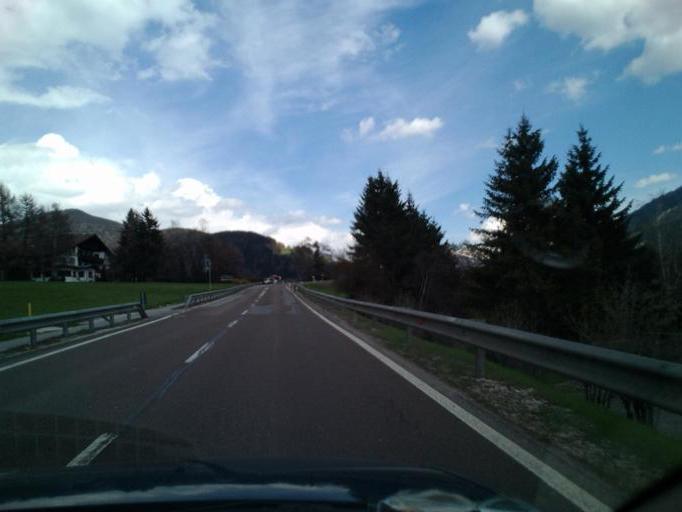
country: IT
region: Trentino-Alto Adige
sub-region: Bolzano
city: Dobbiaco
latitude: 46.7306
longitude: 12.2064
